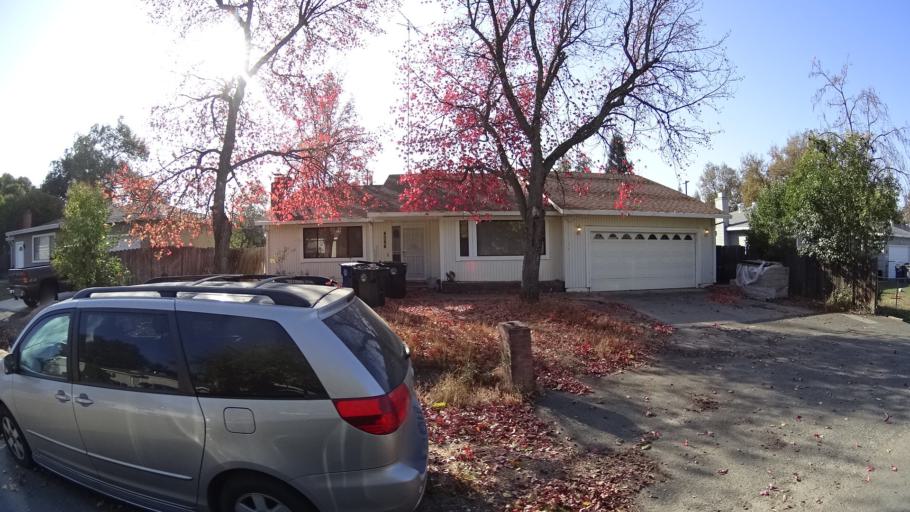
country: US
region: California
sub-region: Sacramento County
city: Citrus Heights
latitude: 38.6971
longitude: -121.2553
